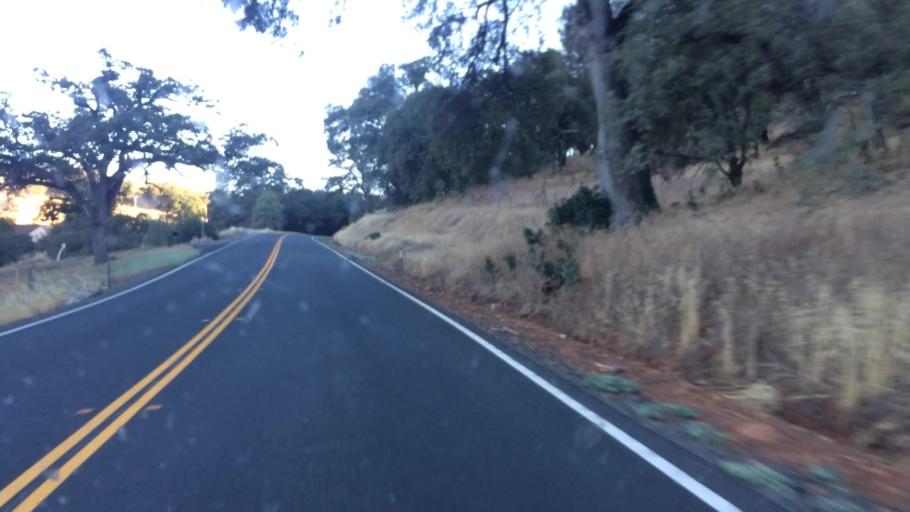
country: US
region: California
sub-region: El Dorado County
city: Deer Park
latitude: 38.6225
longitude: -120.8523
